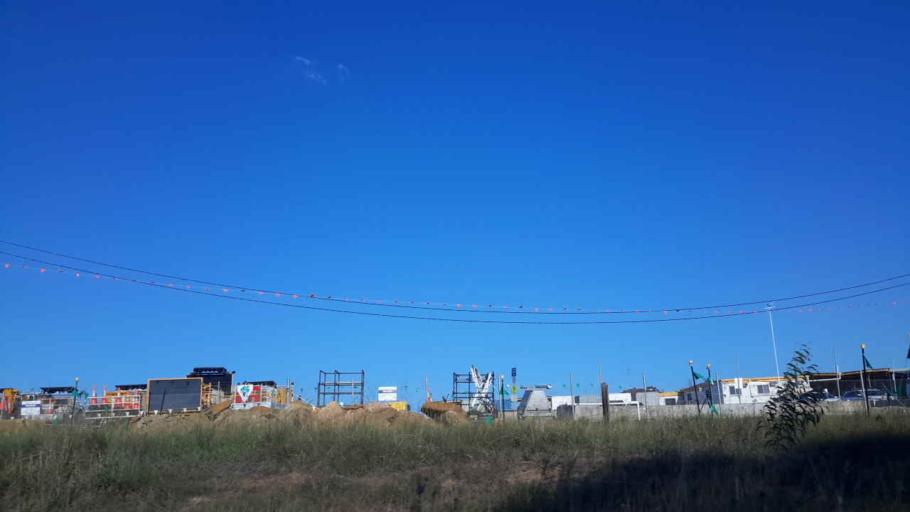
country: AU
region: New South Wales
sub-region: Penrith Municipality
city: Kingswood Park
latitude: -33.7924
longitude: 150.6993
